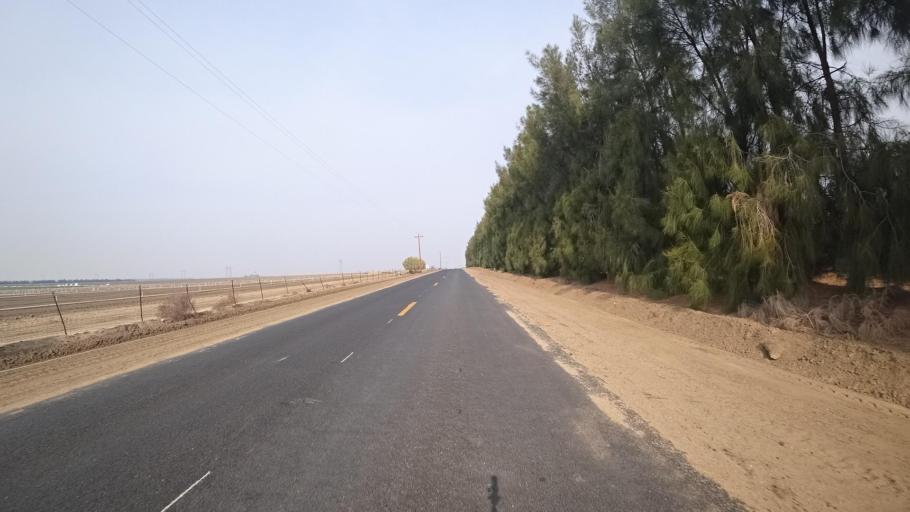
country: US
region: California
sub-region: Kern County
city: Arvin
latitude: 35.1113
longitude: -118.8506
